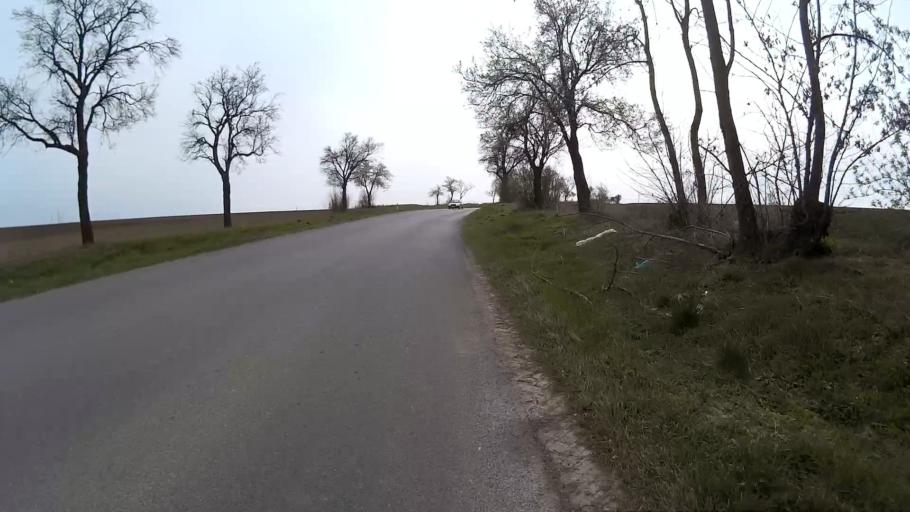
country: CZ
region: South Moravian
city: Orechov
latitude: 49.0742
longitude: 16.5366
